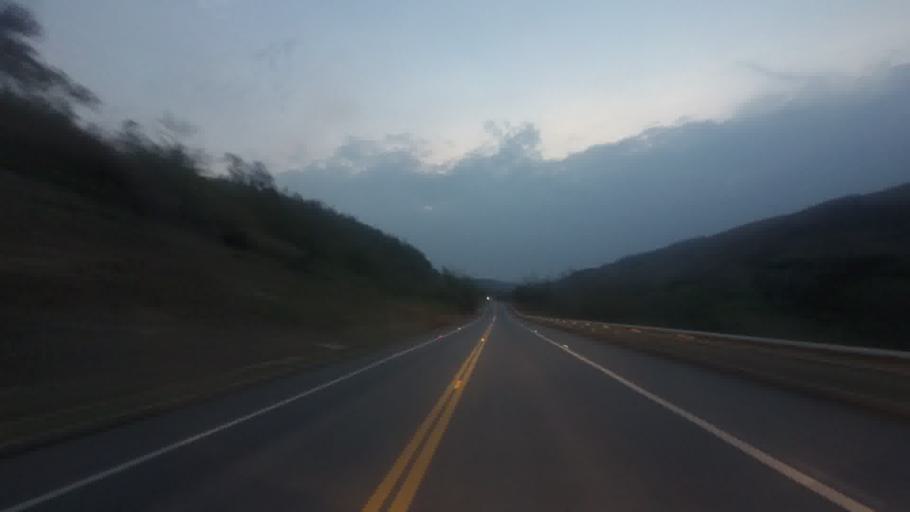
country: BR
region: Minas Gerais
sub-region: Alem Paraiba
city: Alem Paraiba
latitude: -21.9335
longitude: -42.7956
